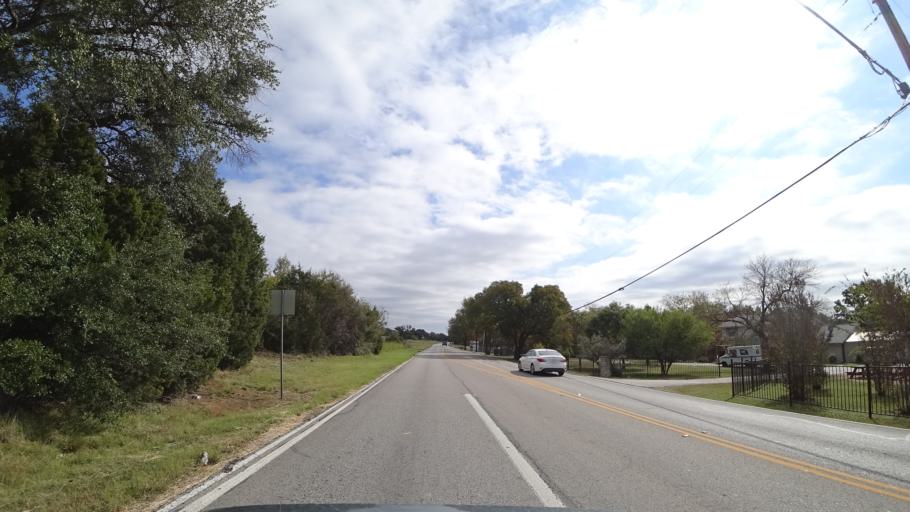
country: US
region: Texas
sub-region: Williamson County
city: Brushy Creek
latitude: 30.5333
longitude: -97.7377
